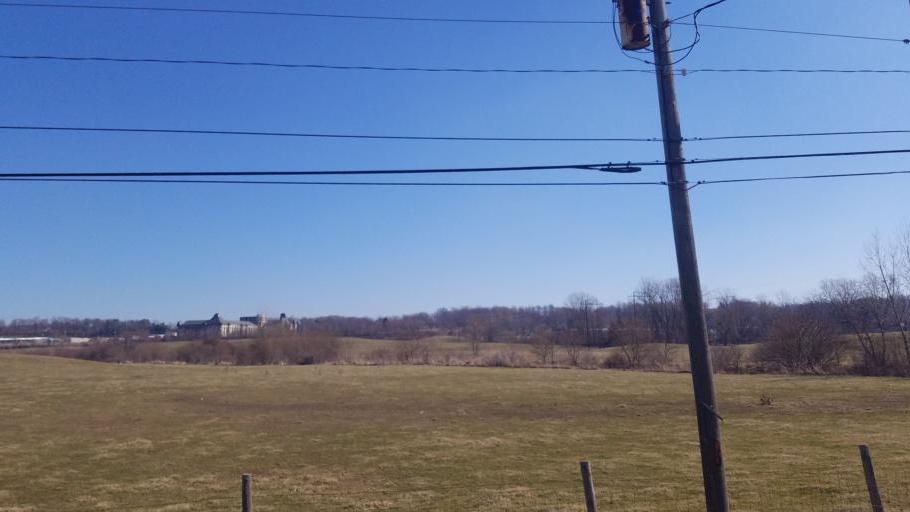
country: US
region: Ohio
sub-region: Richland County
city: Mansfield
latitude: 40.7835
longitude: -82.5136
